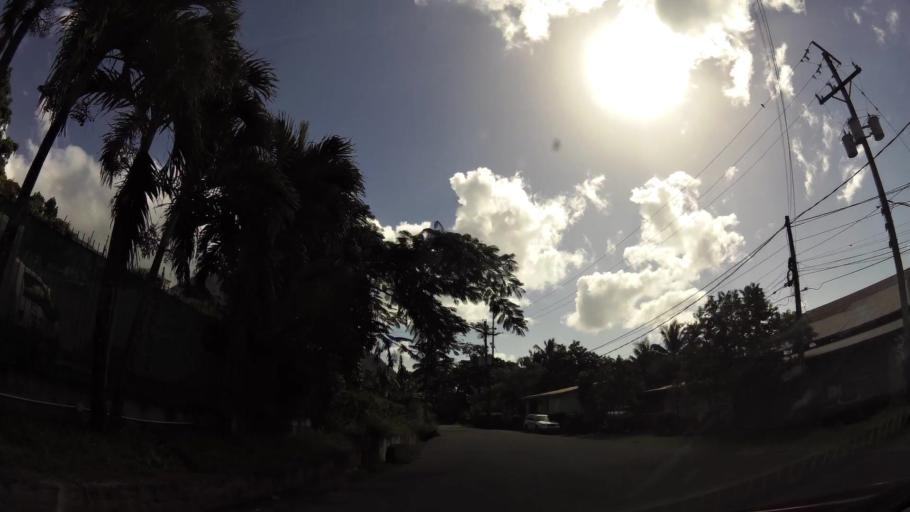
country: DM
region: Saint George
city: Roseau
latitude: 15.2842
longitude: -61.3747
